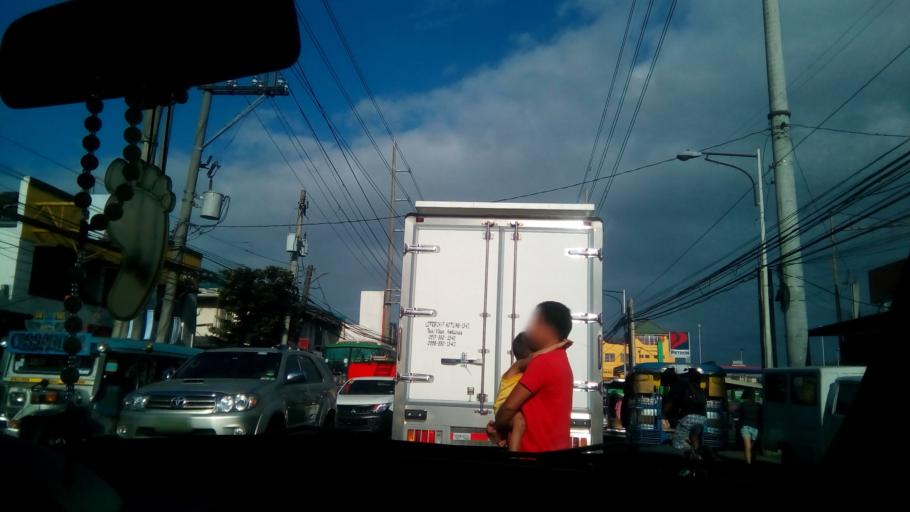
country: PH
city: Sambayanihan People's Village
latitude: 14.4376
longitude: 121.0052
